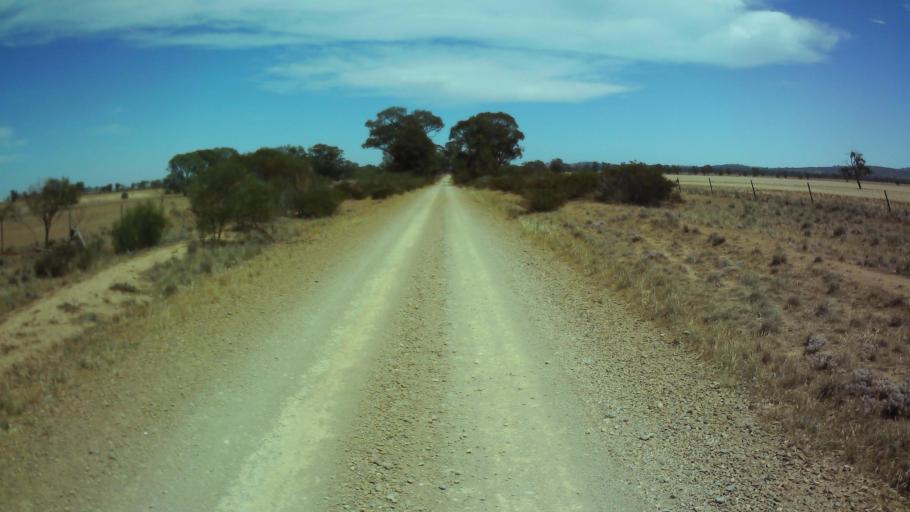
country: AU
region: New South Wales
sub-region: Weddin
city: Grenfell
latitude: -33.8575
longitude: 147.9155
